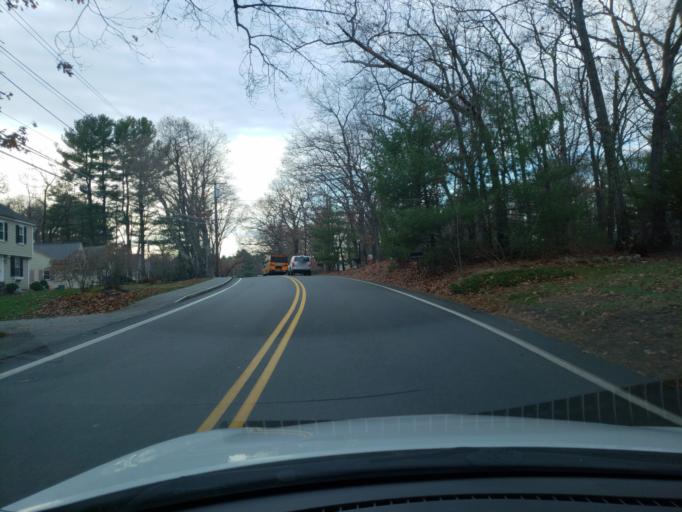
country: US
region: Massachusetts
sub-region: Essex County
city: Andover
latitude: 42.6688
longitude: -71.1750
